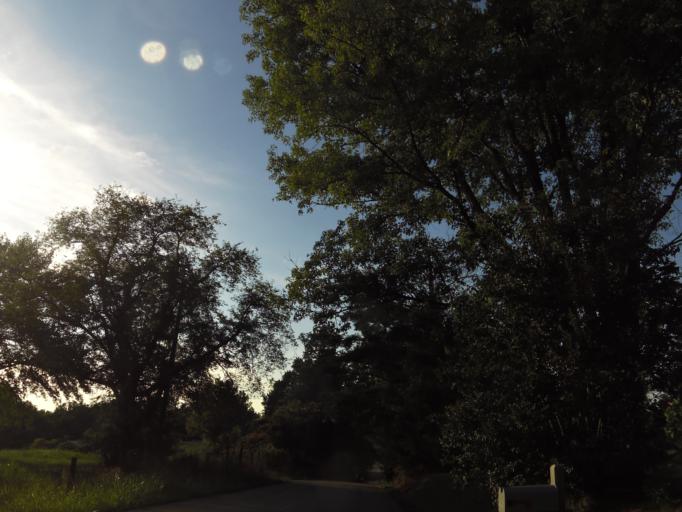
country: US
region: Tennessee
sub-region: Blount County
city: Eagleton Village
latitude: 35.8682
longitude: -83.9216
